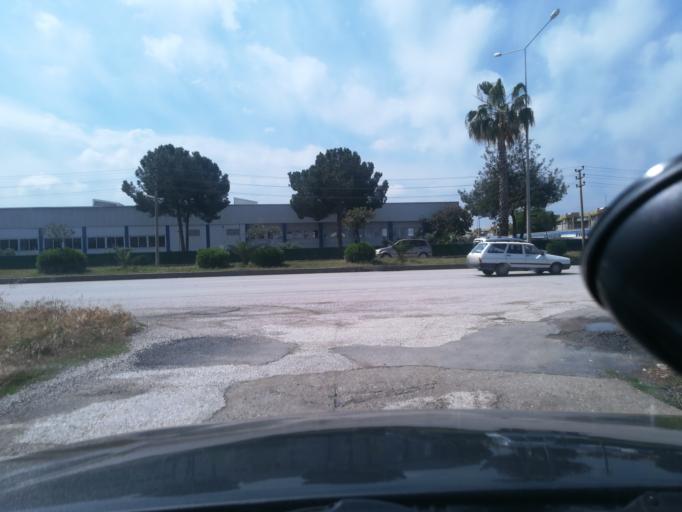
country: TR
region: Adana
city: Yuregir
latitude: 36.9837
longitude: 35.3889
